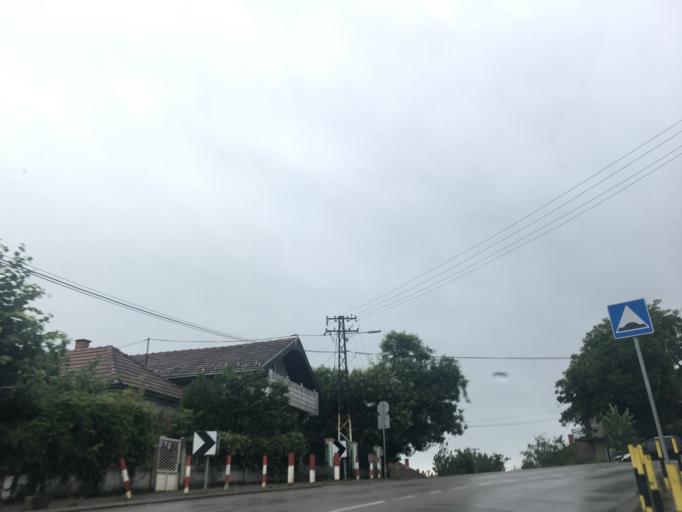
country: RS
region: Central Serbia
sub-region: Nisavski Okrug
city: Aleksinac
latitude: 43.5412
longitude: 21.7027
